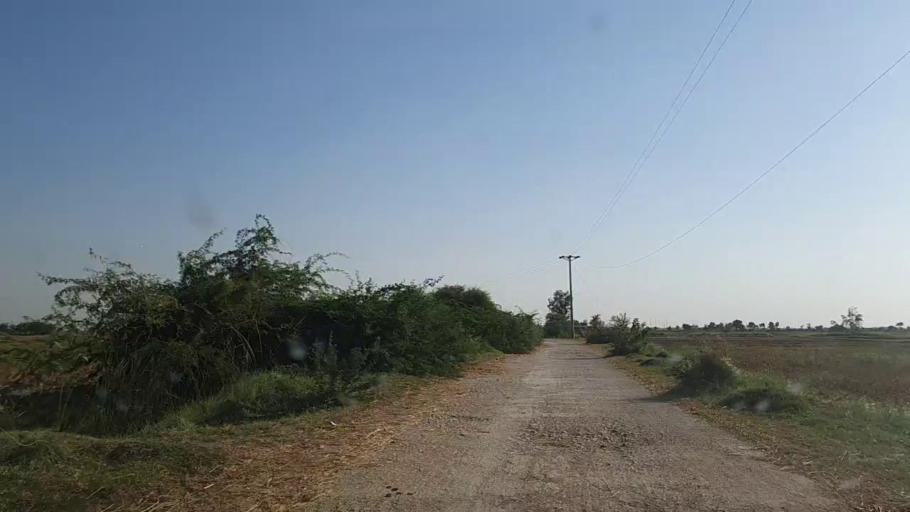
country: PK
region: Sindh
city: Thatta
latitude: 24.6357
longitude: 68.0763
